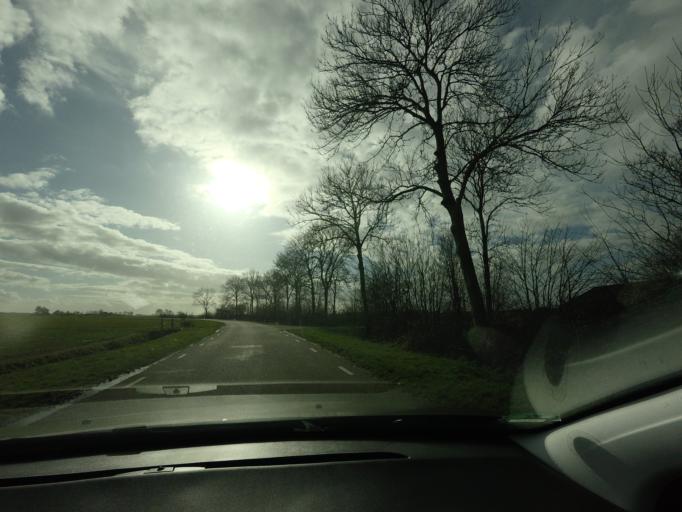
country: NL
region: Friesland
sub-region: Gemeente Boarnsterhim
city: Jirnsum
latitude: 53.0645
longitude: 5.7425
